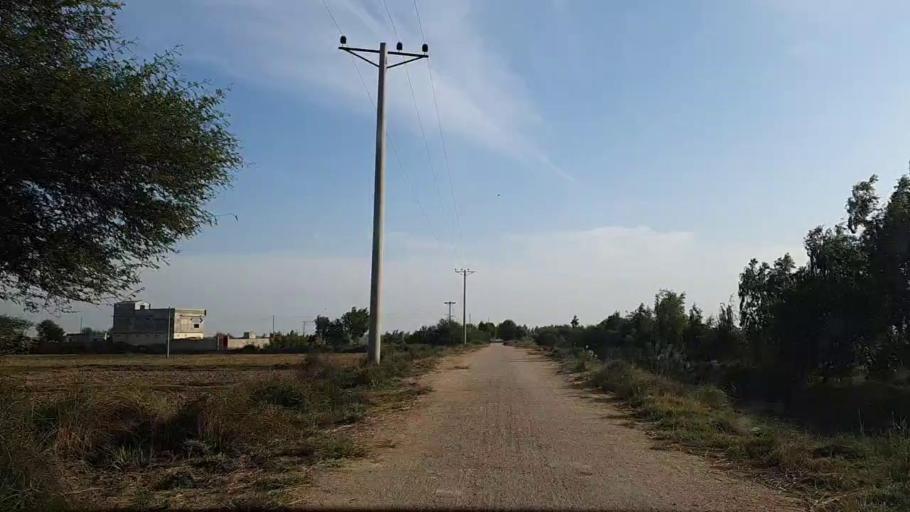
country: PK
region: Sindh
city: Daro Mehar
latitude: 24.6705
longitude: 68.1159
